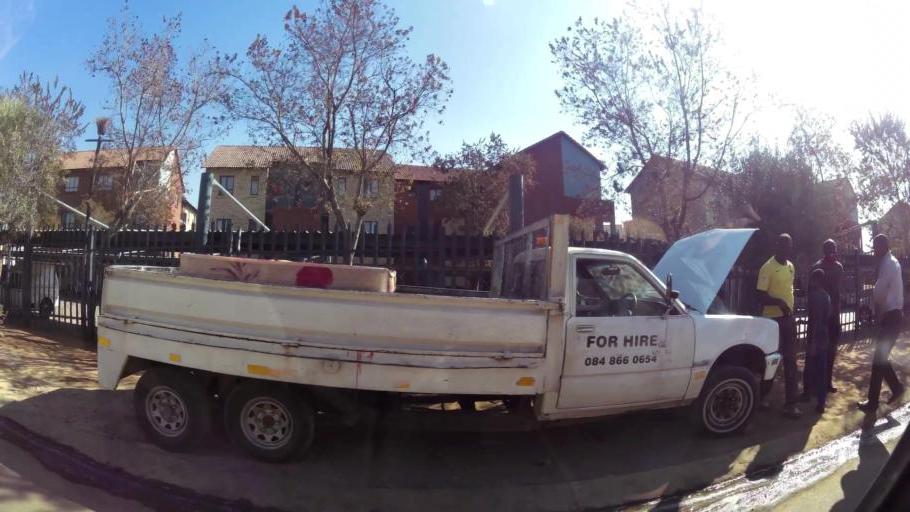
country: ZA
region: Gauteng
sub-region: West Rand District Municipality
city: Muldersdriseloop
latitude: -26.0224
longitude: 27.9250
